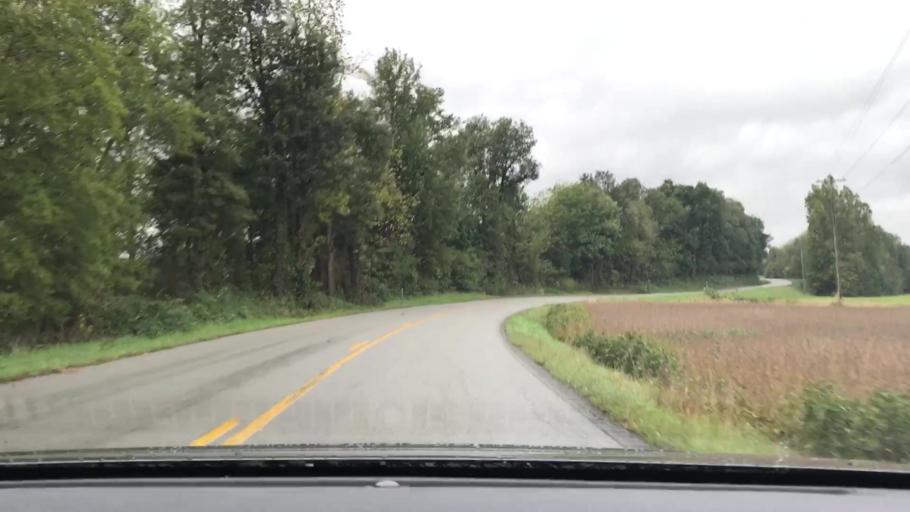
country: US
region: Kentucky
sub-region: McLean County
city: Calhoun
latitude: 37.4501
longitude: -87.2382
